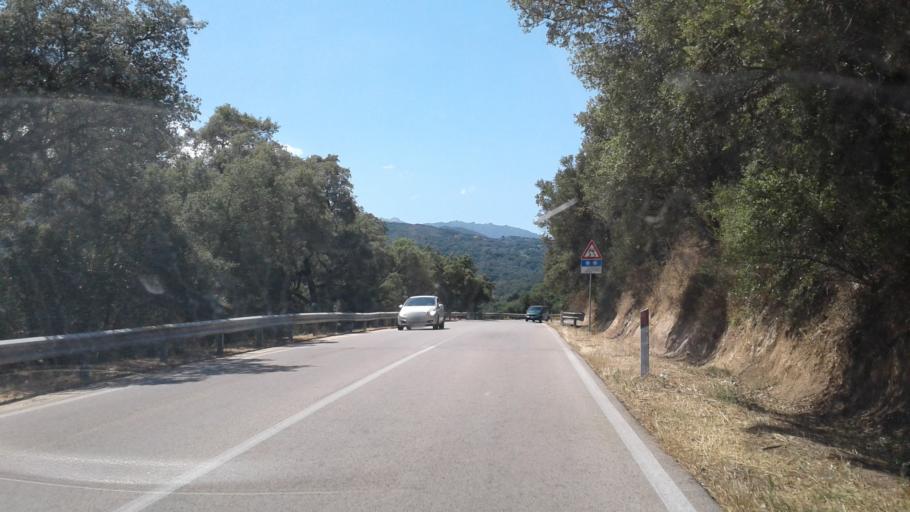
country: IT
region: Sardinia
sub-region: Provincia di Olbia-Tempio
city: Luras
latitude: 40.9508
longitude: 9.2019
